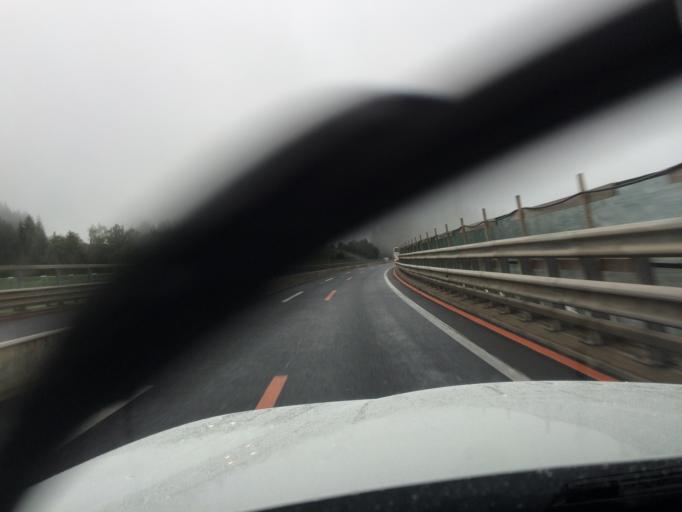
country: AT
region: Styria
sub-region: Politischer Bezirk Voitsberg
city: Voitsberg
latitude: 46.9764
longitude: 15.1157
